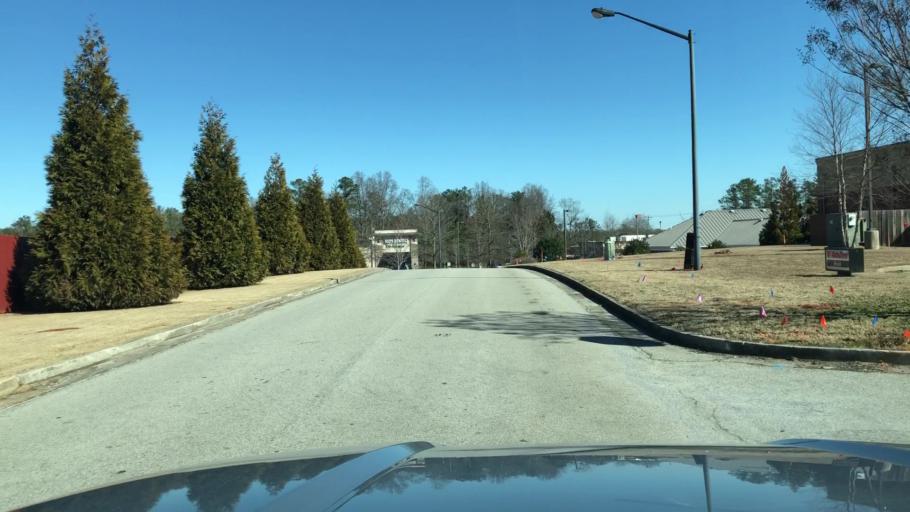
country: US
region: Georgia
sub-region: Cobb County
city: Acworth
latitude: 34.0114
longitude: -84.7557
